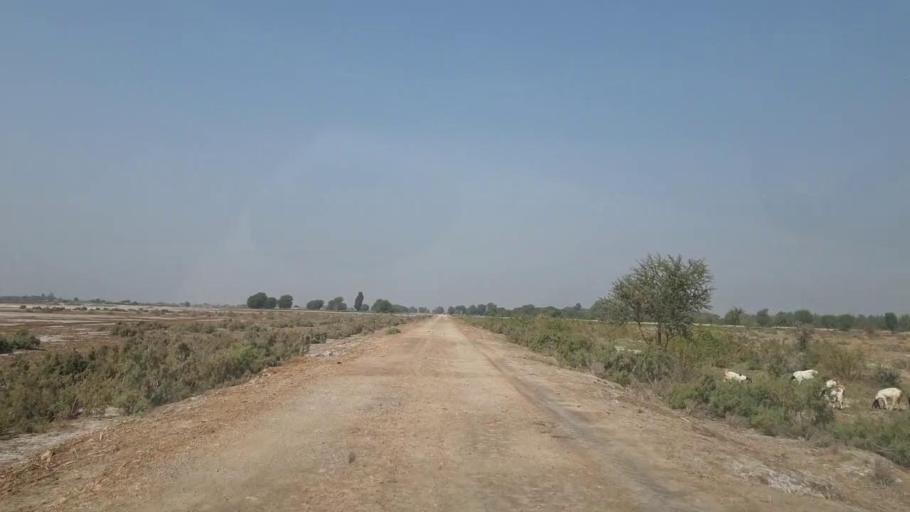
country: PK
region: Sindh
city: Mirpur Khas
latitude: 25.6528
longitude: 69.1376
